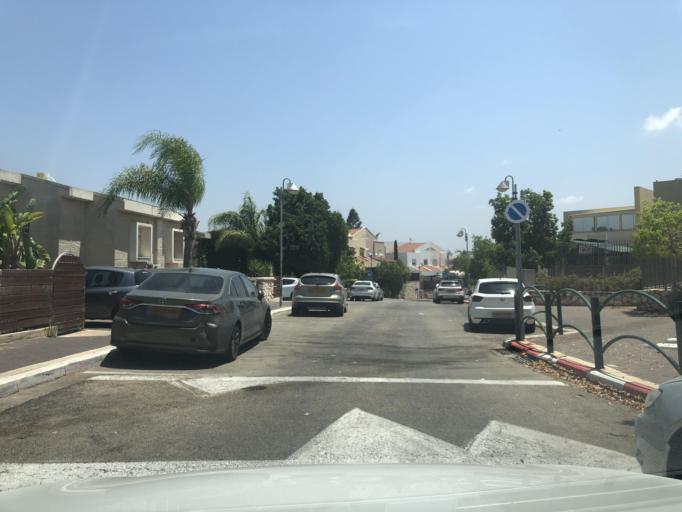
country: IL
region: Haifa
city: Daliyat el Karmil
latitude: 32.6392
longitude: 35.0908
